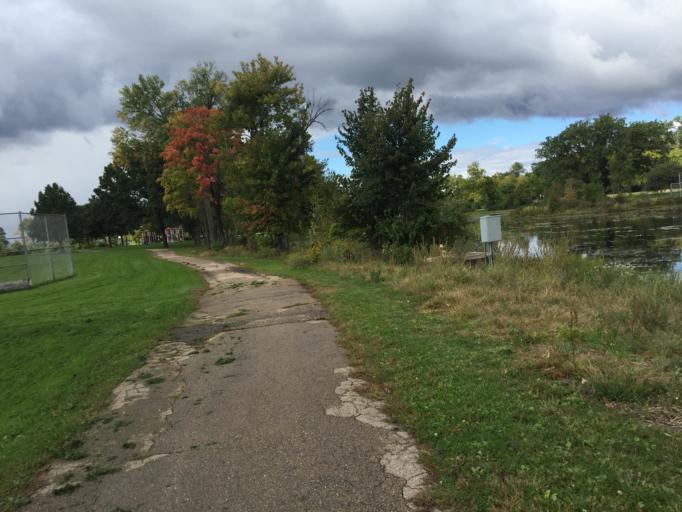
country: US
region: Wisconsin
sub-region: Dane County
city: Maple Bluff
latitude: 43.0918
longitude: -89.3680
